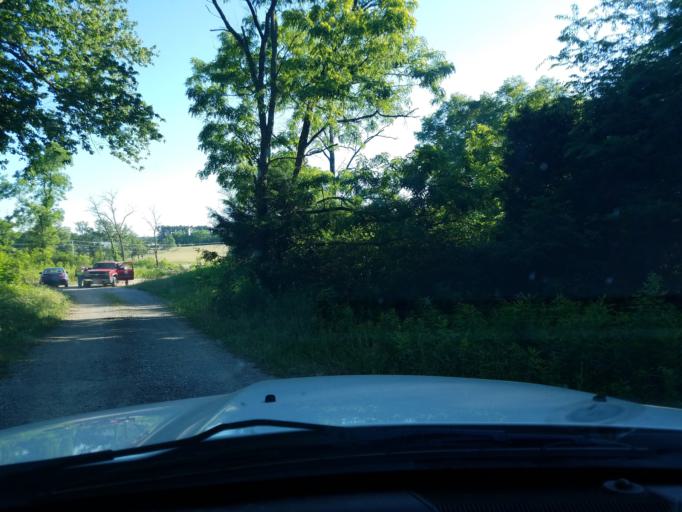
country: US
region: Tennessee
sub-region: Putnam County
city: Baxter
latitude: 36.1369
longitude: -85.5738
